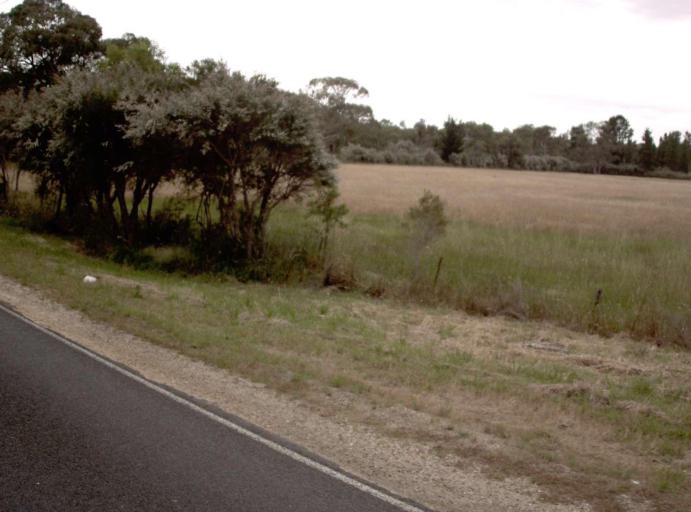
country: AU
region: Victoria
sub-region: Wellington
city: Sale
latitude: -38.1807
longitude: 147.1336
